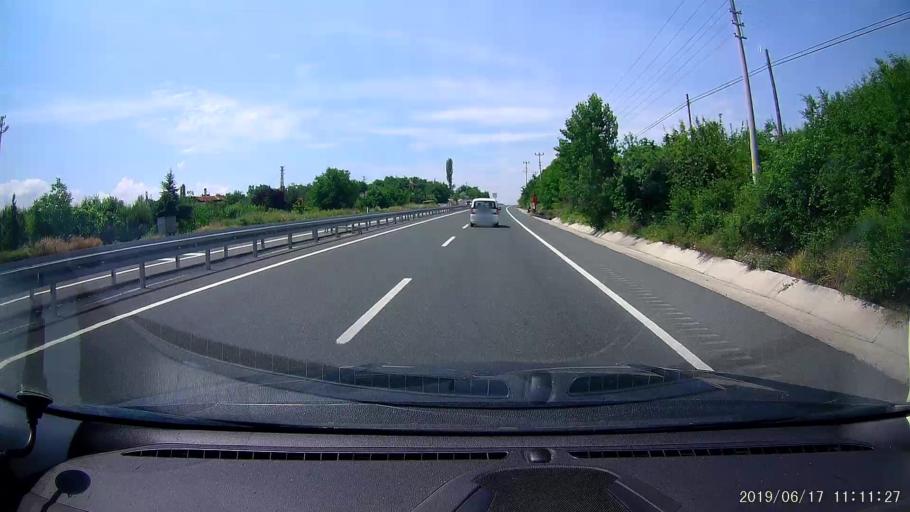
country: TR
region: Kastamonu
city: Tosya
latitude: 40.9865
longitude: 34.0091
